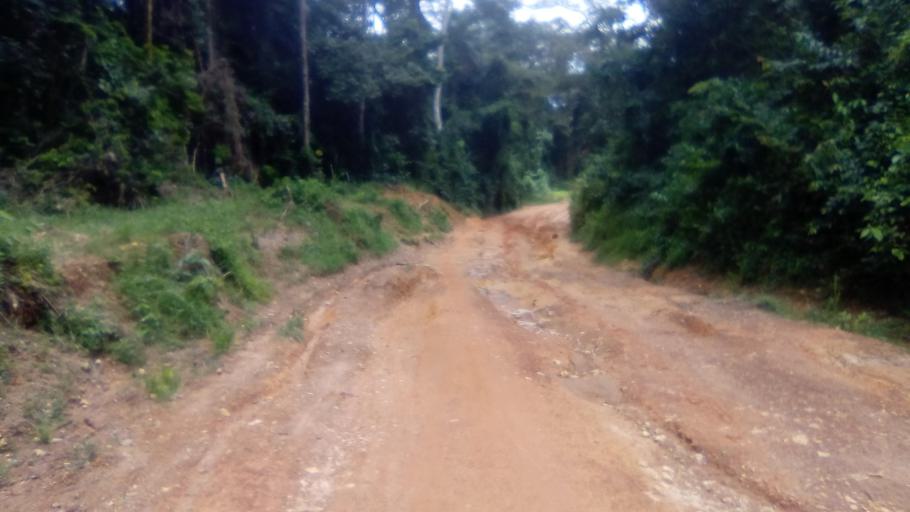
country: SL
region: Eastern Province
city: Simbakoro
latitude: 8.5292
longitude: -10.9101
